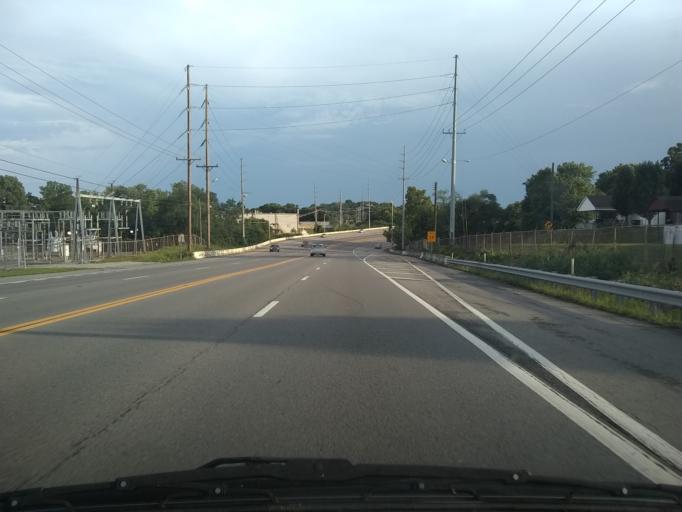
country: US
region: Tennessee
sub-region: Davidson County
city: Oak Hill
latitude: 36.1221
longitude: -86.6967
